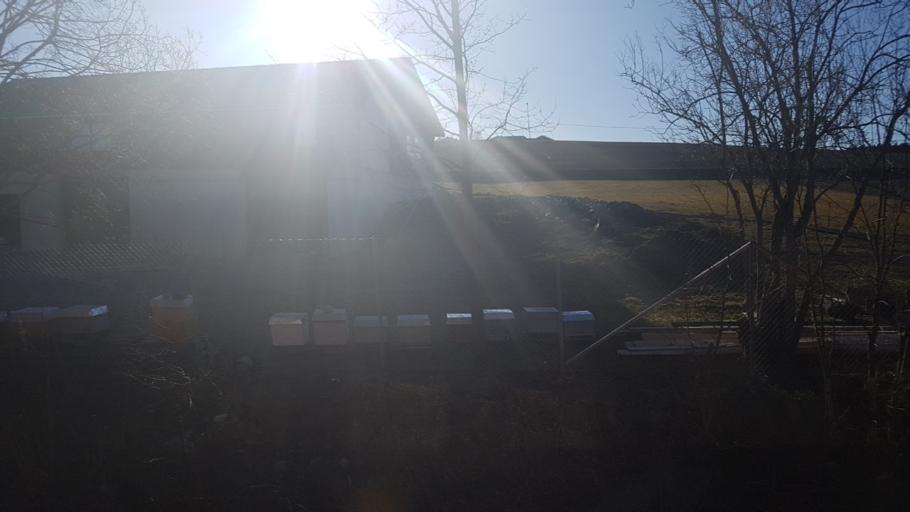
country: NO
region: Nord-Trondelag
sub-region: Levanger
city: Skogn
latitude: 63.6739
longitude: 11.1033
